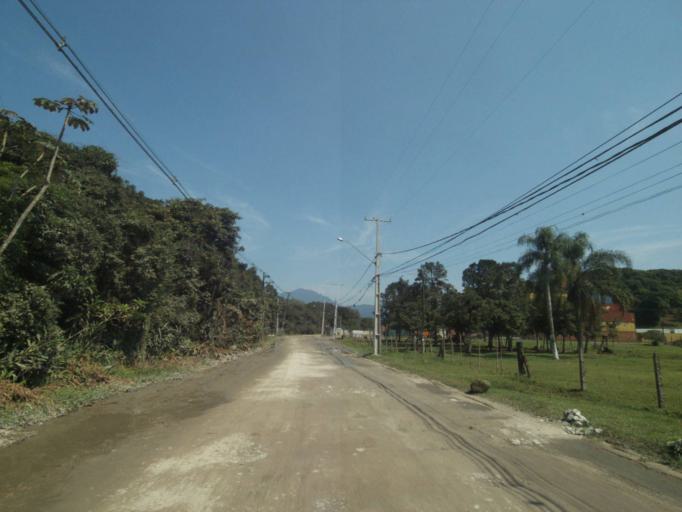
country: BR
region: Parana
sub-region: Paranagua
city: Paranagua
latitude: -25.5524
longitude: -48.5888
